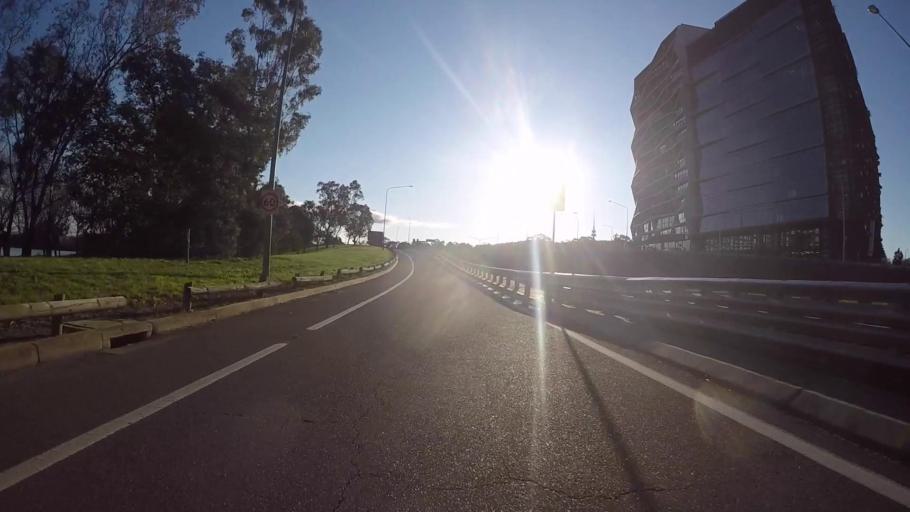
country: AU
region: Australian Capital Territory
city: Canberra
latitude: -35.2858
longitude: 149.1239
